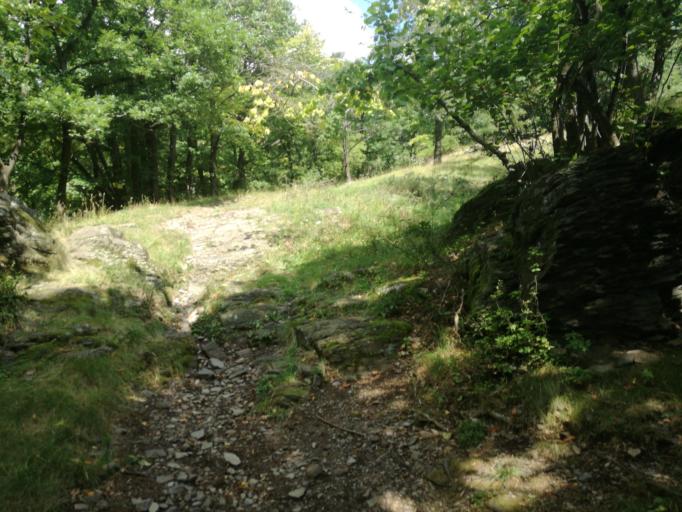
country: HU
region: Heves
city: Paradsasvar
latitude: 47.8544
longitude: 19.9829
